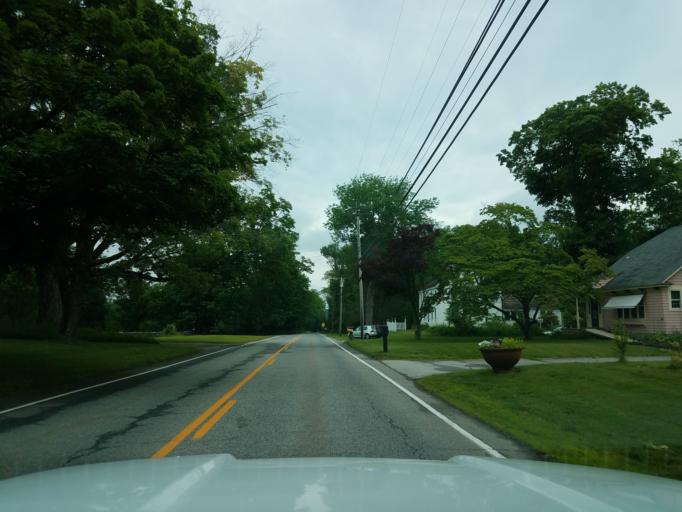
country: US
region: Connecticut
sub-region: Windham County
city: South Windham
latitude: 41.6385
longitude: -72.2097
